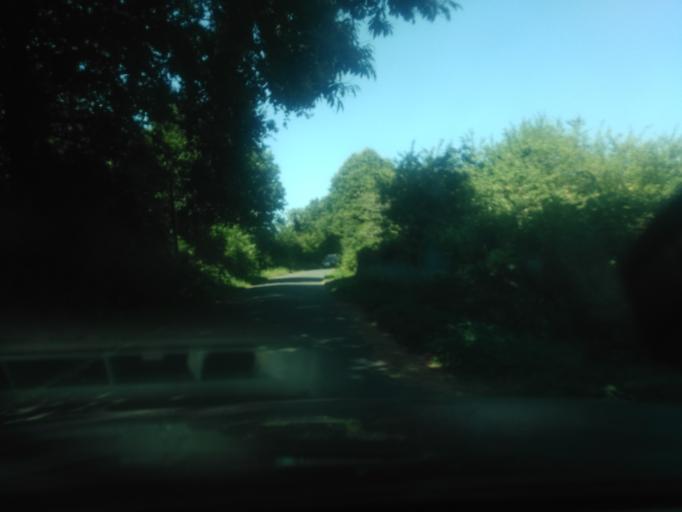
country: FR
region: Pays de la Loire
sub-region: Departement de la Vendee
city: Dompierre-sur-Yon
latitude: 46.7223
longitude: -1.3747
